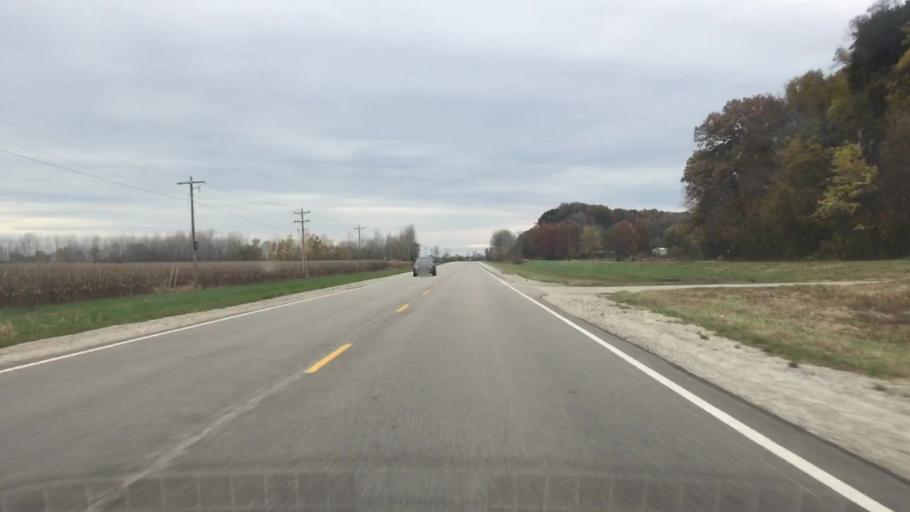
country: US
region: Missouri
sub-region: Callaway County
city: Holts Summit
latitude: 38.5818
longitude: -92.1049
